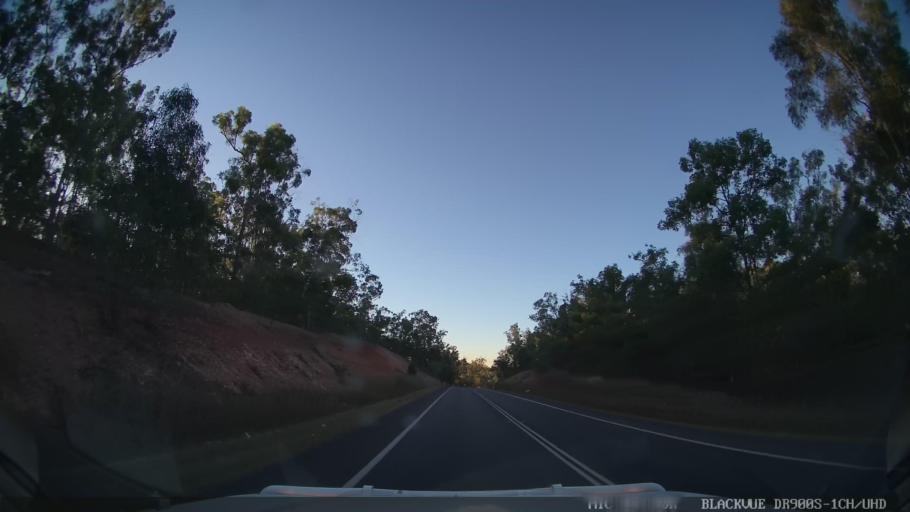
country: AU
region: Queensland
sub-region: Gladstone
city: Toolooa
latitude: -23.9653
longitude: 151.2175
